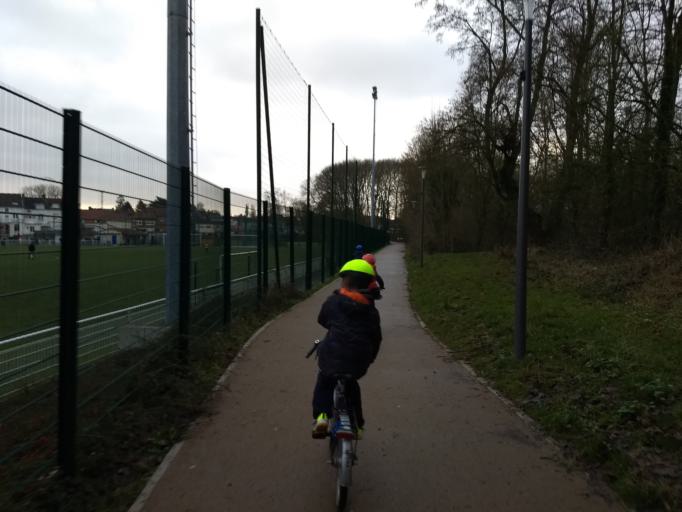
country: FR
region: Nord-Pas-de-Calais
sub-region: Departement du Pas-de-Calais
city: Achicourt
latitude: 50.2829
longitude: 2.7646
